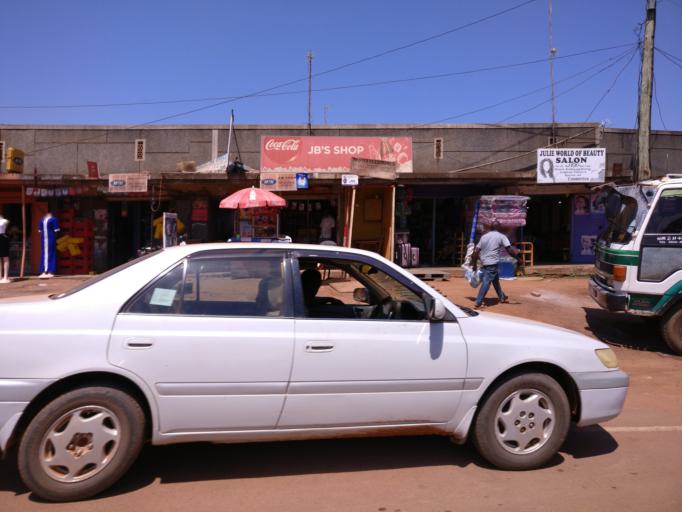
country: UG
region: Central Region
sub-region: Wakiso District
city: Entebbe
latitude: 0.1061
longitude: 32.5190
